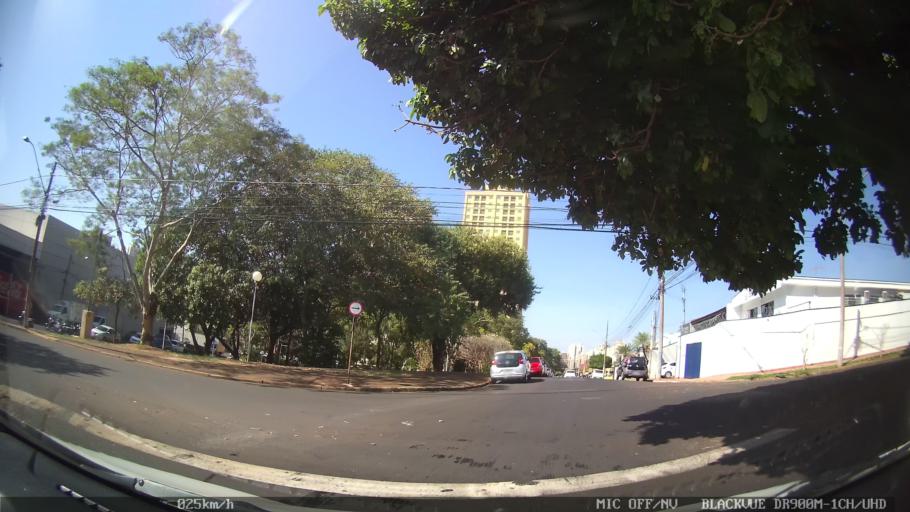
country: BR
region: Sao Paulo
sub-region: Ribeirao Preto
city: Ribeirao Preto
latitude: -21.1923
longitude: -47.8031
